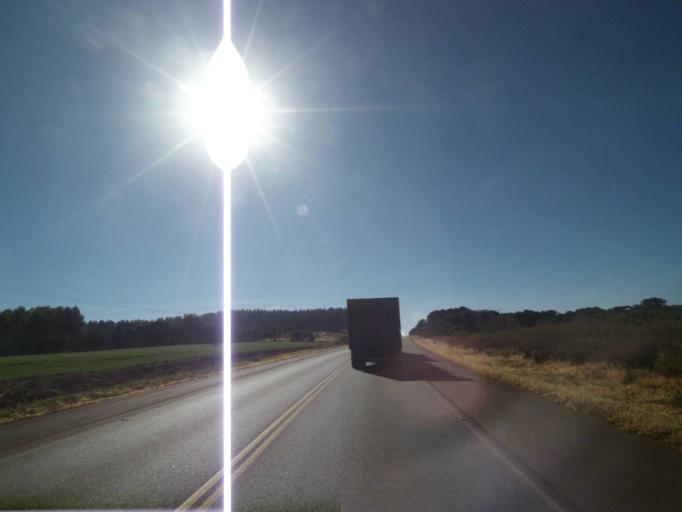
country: BR
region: Parana
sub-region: Tibagi
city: Tibagi
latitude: -24.4368
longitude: -50.4207
